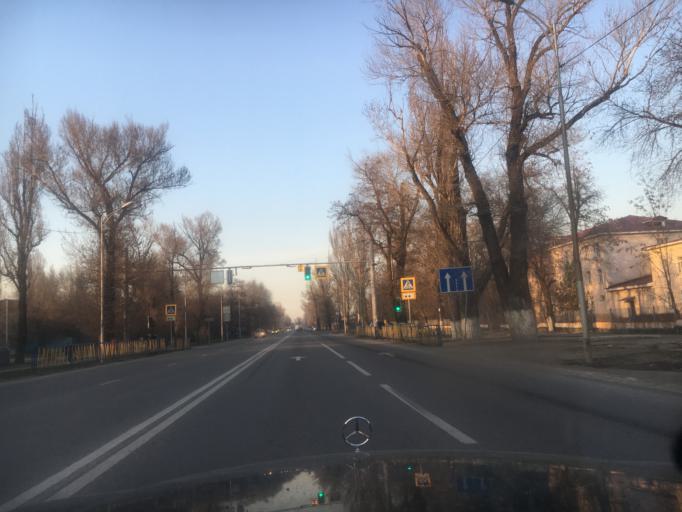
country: KZ
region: Almaty Oblysy
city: Pervomayskiy
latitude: 43.3734
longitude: 76.9909
